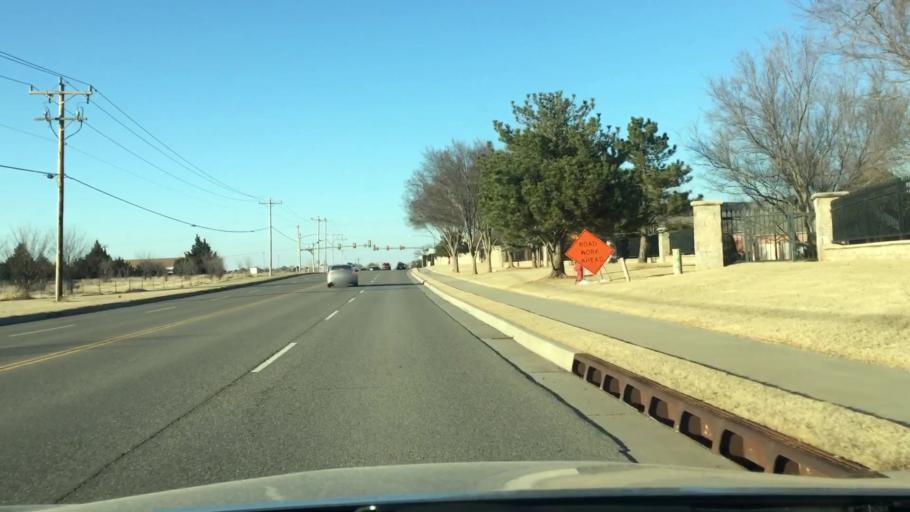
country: US
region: Oklahoma
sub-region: Oklahoma County
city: The Village
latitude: 35.6215
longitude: -97.6208
